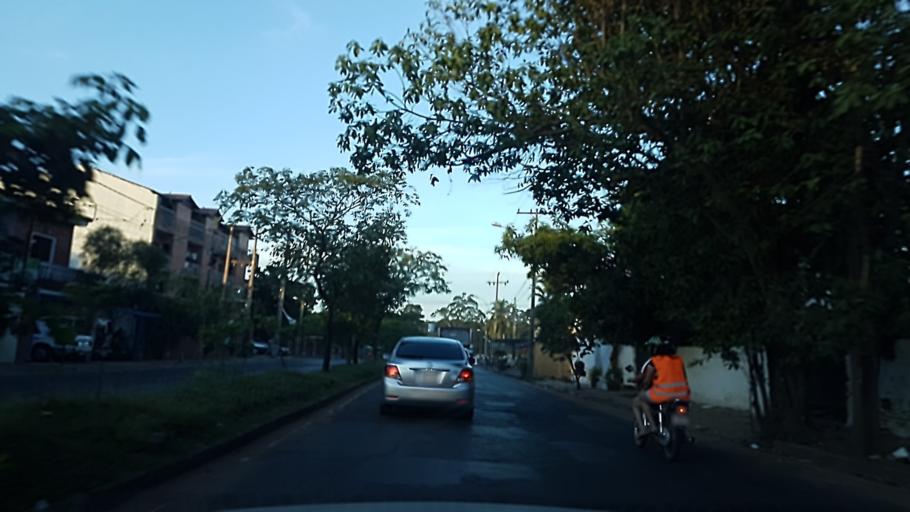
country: PY
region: Asuncion
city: Asuncion
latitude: -25.2558
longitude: -57.5774
